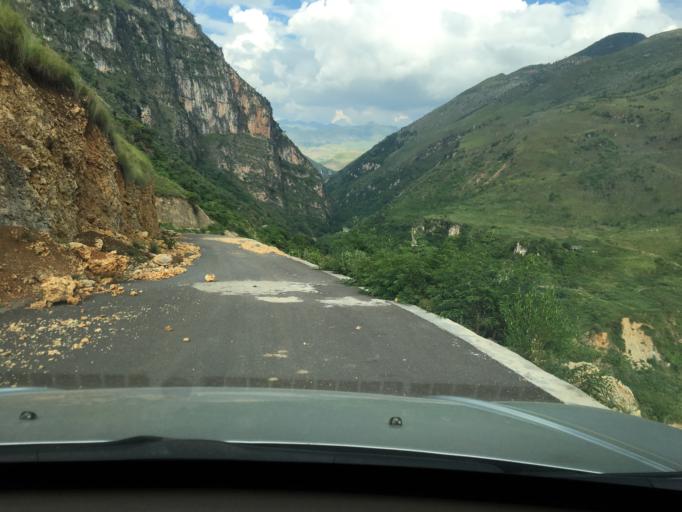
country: CN
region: Guizhou Sheng
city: Anshun
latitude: 25.7777
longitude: 105.3879
